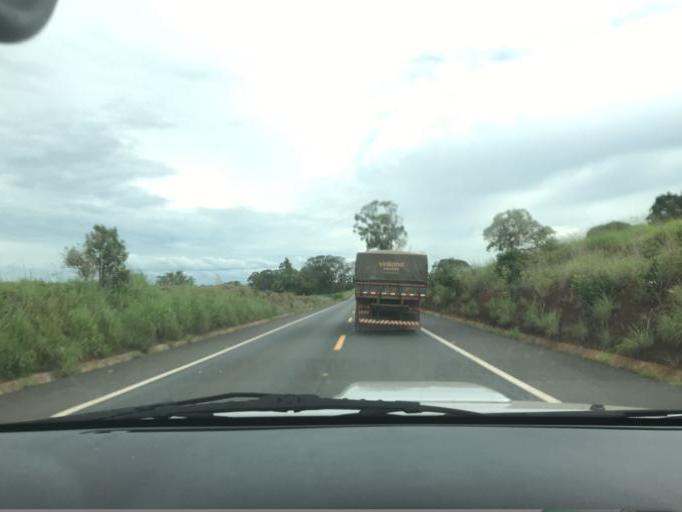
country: BR
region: Minas Gerais
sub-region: Araxa
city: Araxa
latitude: -19.3722
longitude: -46.8564
